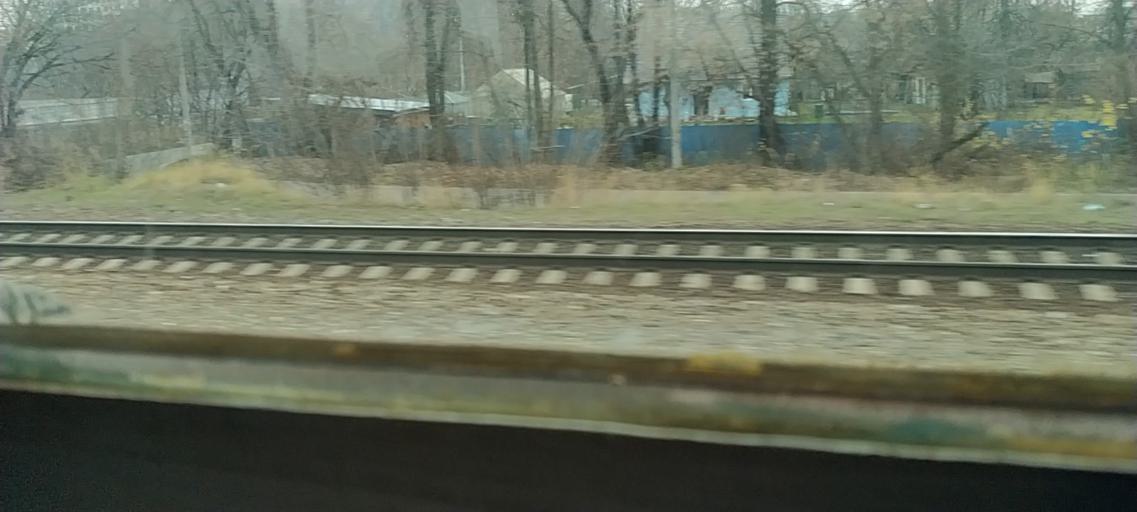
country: RU
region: Moskovskaya
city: Korenevo
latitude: 55.6685
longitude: 37.9974
